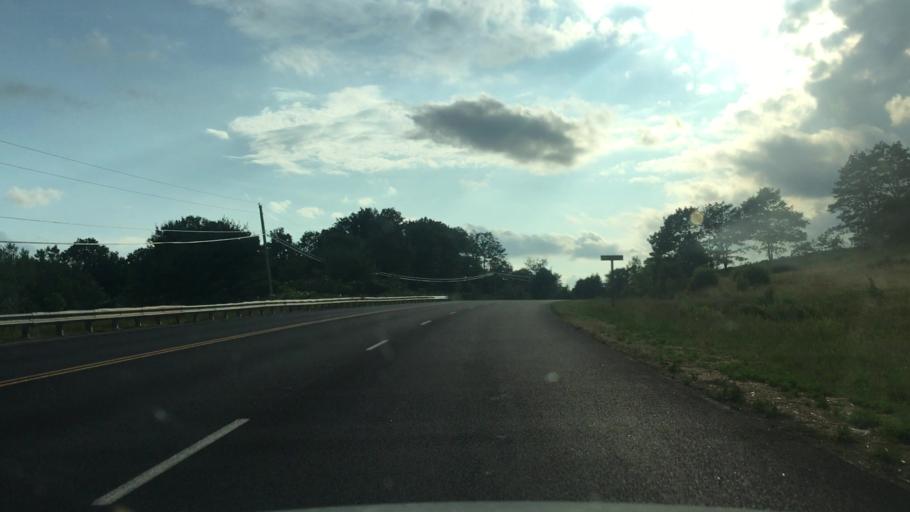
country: US
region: Maine
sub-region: Waldo County
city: Palermo
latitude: 44.3763
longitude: -69.4432
